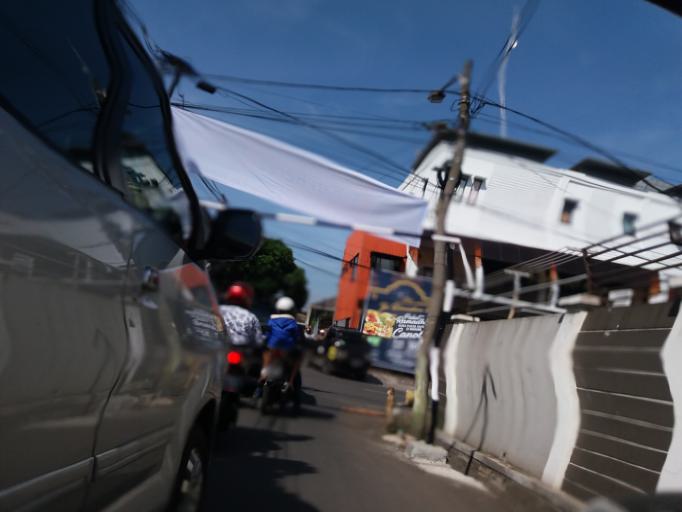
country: ID
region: West Java
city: Bandung
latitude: -6.9432
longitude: 107.6126
